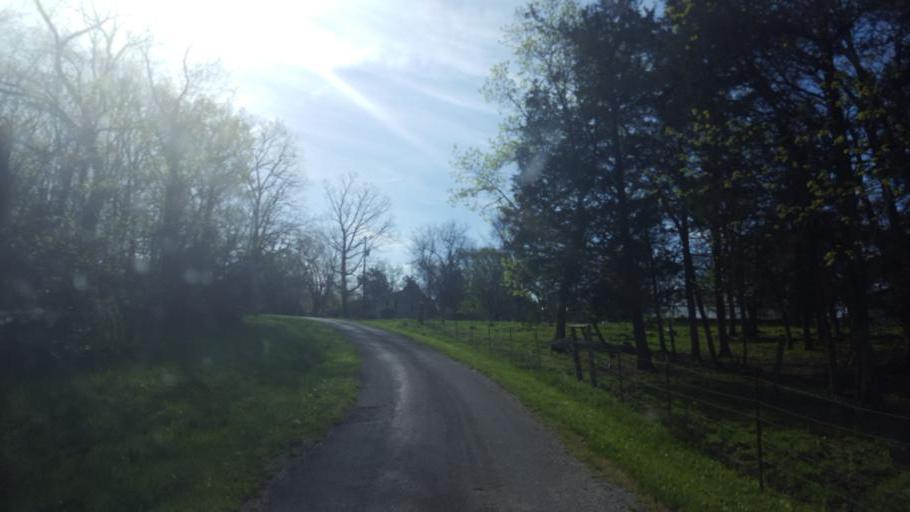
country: US
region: Kentucky
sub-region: Edmonson County
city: Brownsville
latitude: 37.3285
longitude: -86.1083
